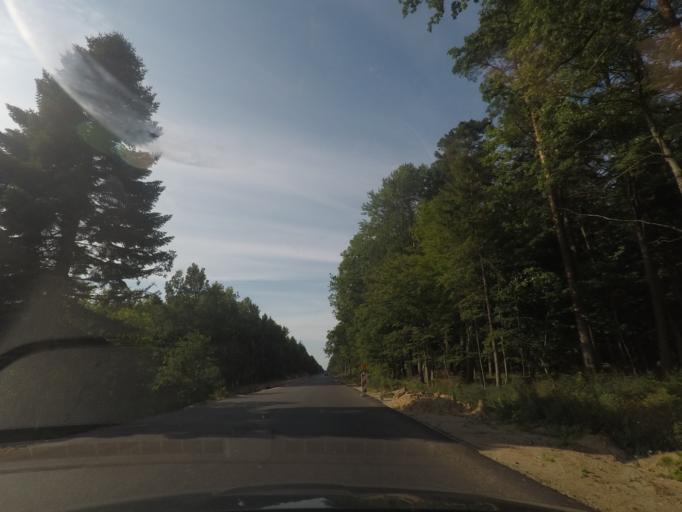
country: PL
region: Pomeranian Voivodeship
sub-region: Powiat leborski
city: Leba
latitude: 54.6960
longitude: 17.5907
